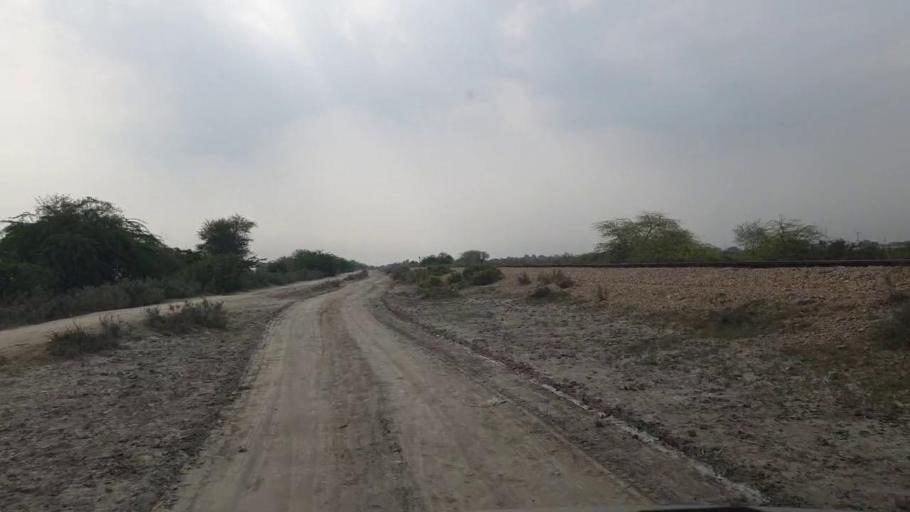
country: PK
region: Sindh
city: Talhar
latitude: 24.8615
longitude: 68.8185
